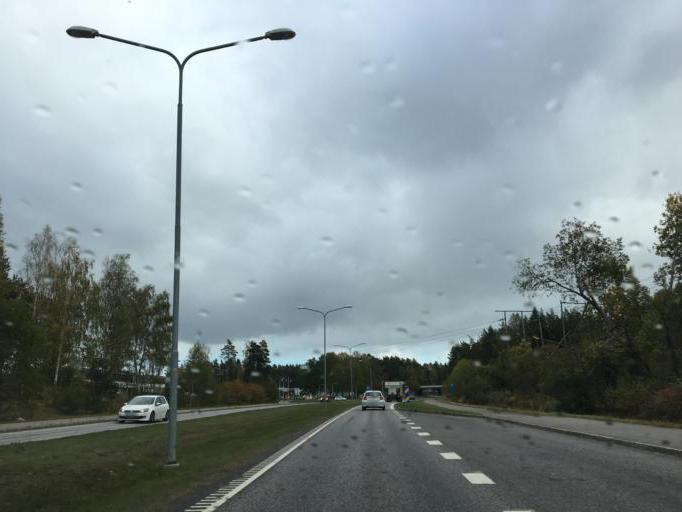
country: SE
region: Soedermanland
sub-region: Nykopings Kommun
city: Nykoping
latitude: 58.7653
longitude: 16.9844
